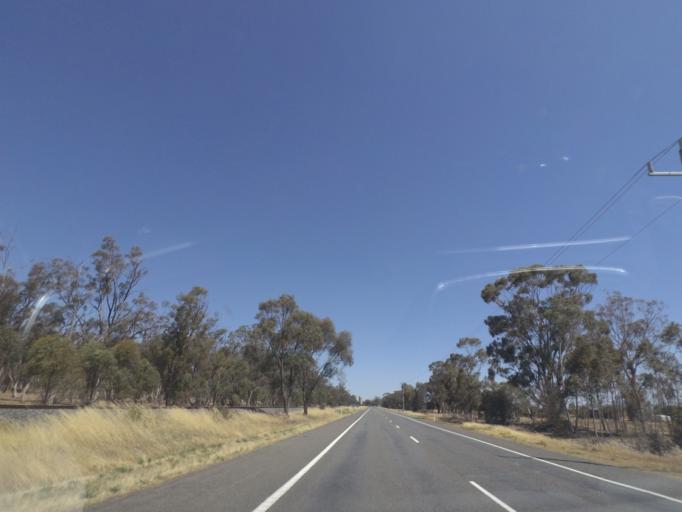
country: AU
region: Victoria
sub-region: Greater Shepparton
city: Shepparton
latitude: -36.2277
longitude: 145.4318
